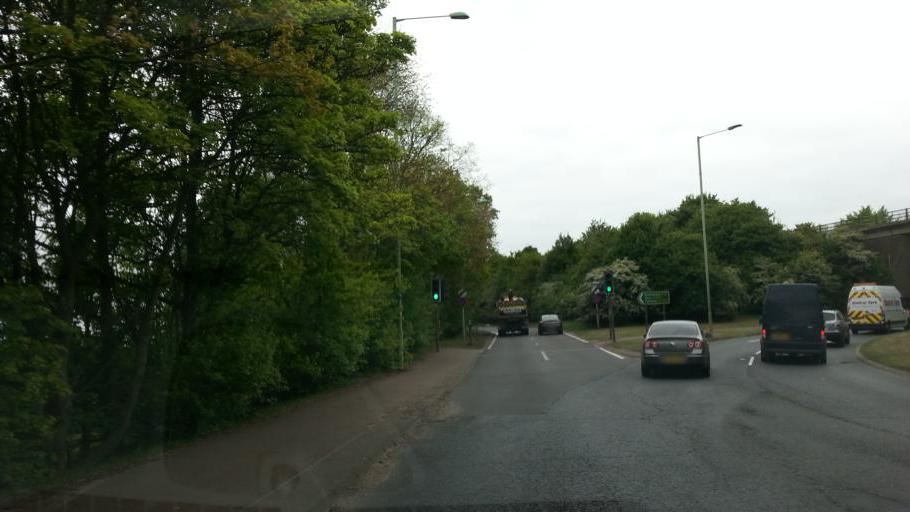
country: GB
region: England
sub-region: Suffolk
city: Bury St Edmunds
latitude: 52.2387
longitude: 0.7321
